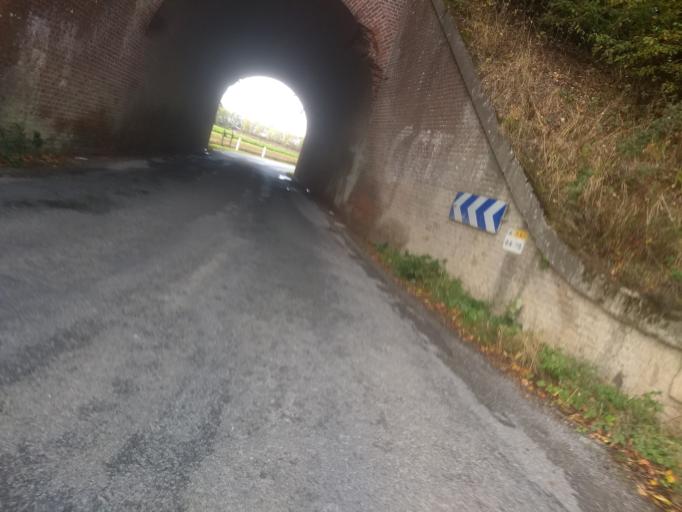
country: FR
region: Nord-Pas-de-Calais
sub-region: Departement du Pas-de-Calais
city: Dainville
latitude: 50.2818
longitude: 2.7090
